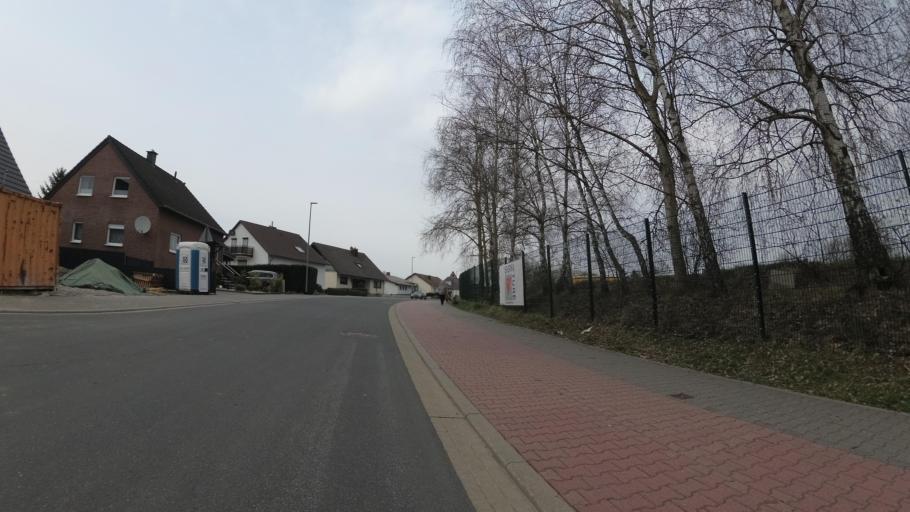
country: DE
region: Rheinland-Pfalz
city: Birkenfeld
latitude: 49.6541
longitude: 7.1581
